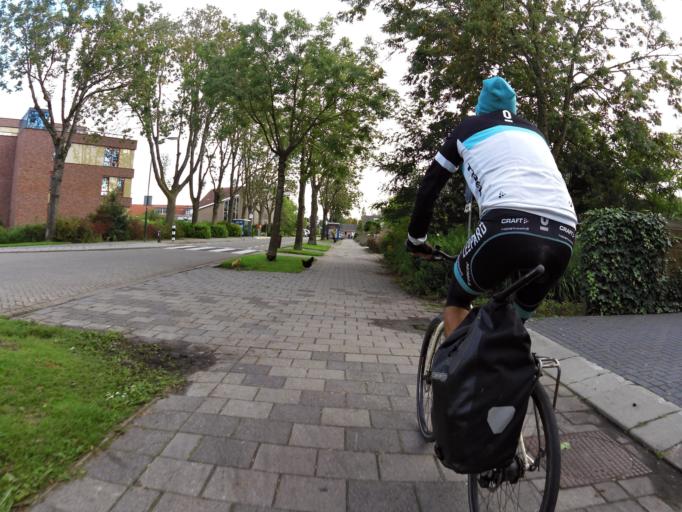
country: NL
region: Utrecht
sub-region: Stichtse Vecht
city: Breukelen
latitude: 52.1487
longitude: 4.9493
